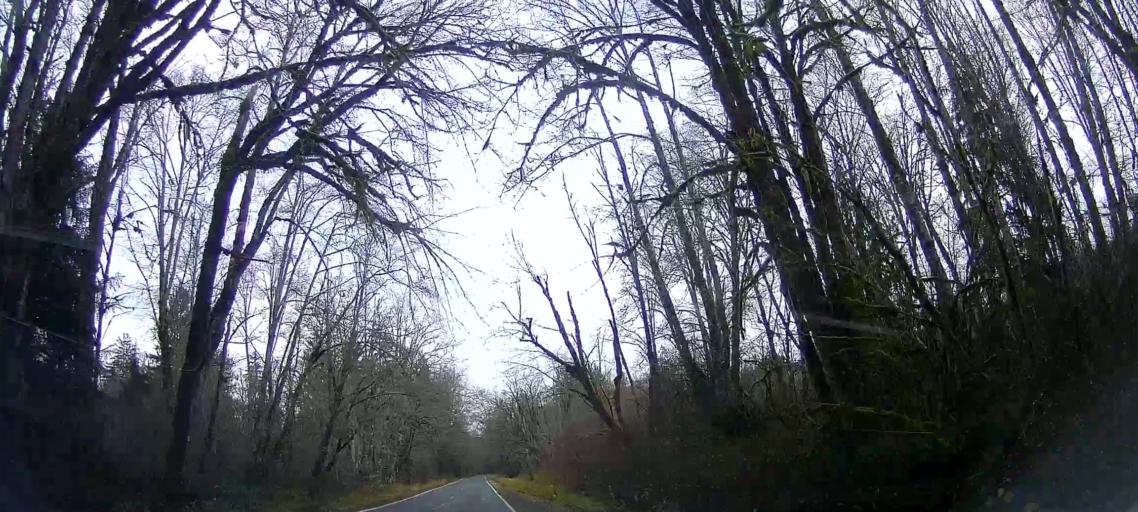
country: US
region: Washington
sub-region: Skagit County
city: Sedro-Woolley
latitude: 48.5149
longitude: -121.8732
